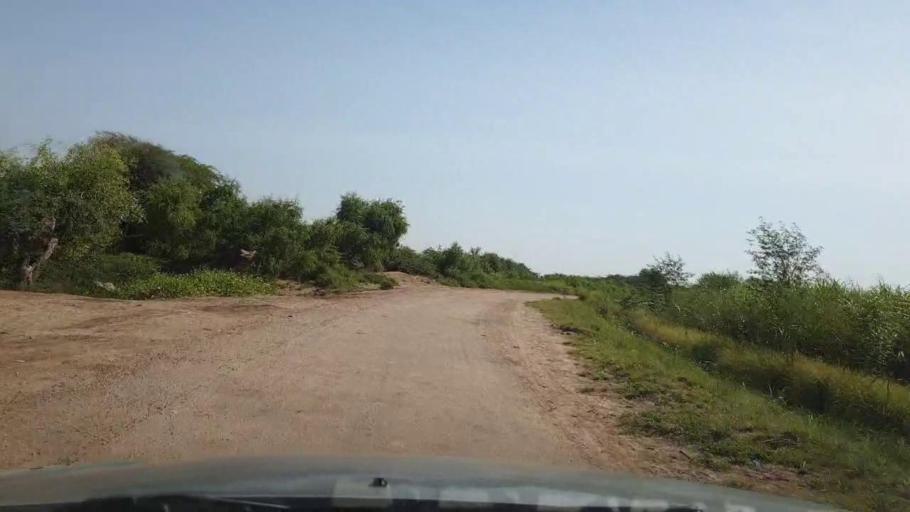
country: PK
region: Sindh
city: Bulri
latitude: 25.0149
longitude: 68.3194
